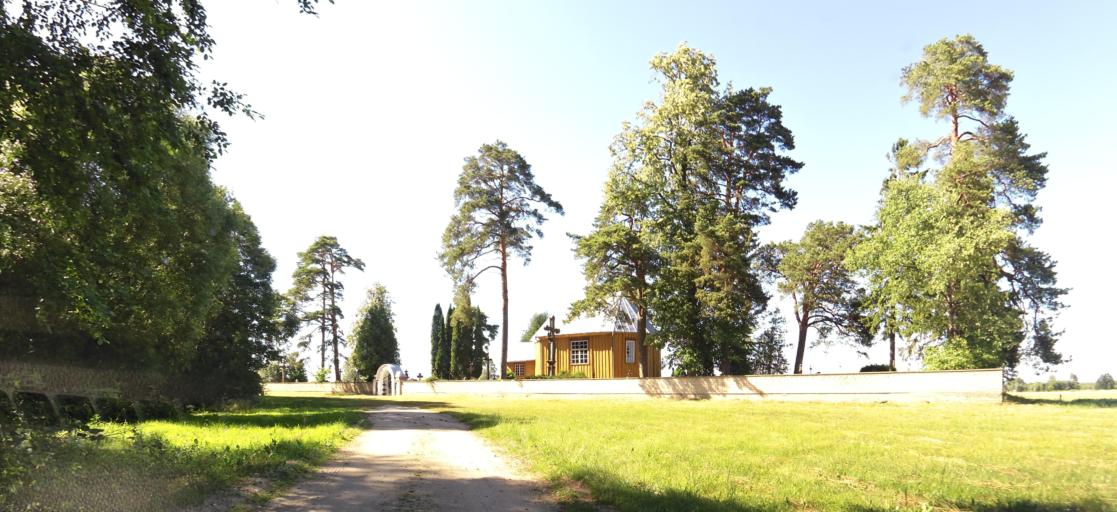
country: LT
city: Vabalninkas
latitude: 56.0248
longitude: 24.7135
